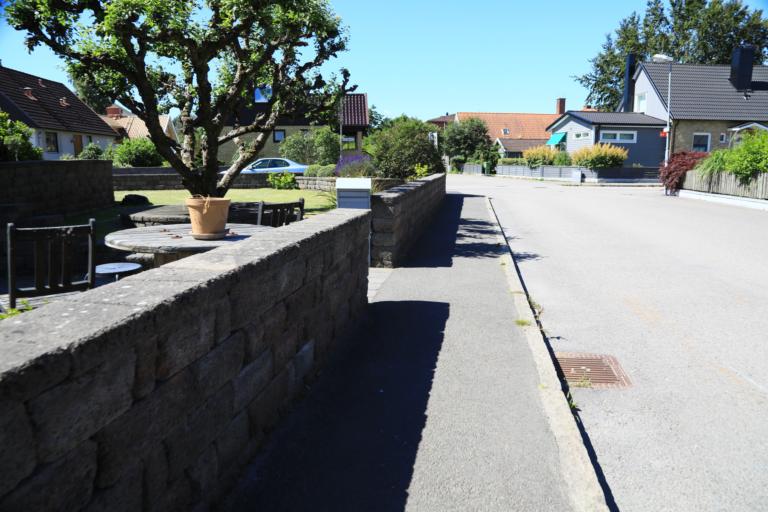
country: SE
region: Halland
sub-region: Varbergs Kommun
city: Varberg
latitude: 57.1067
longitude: 12.2669
